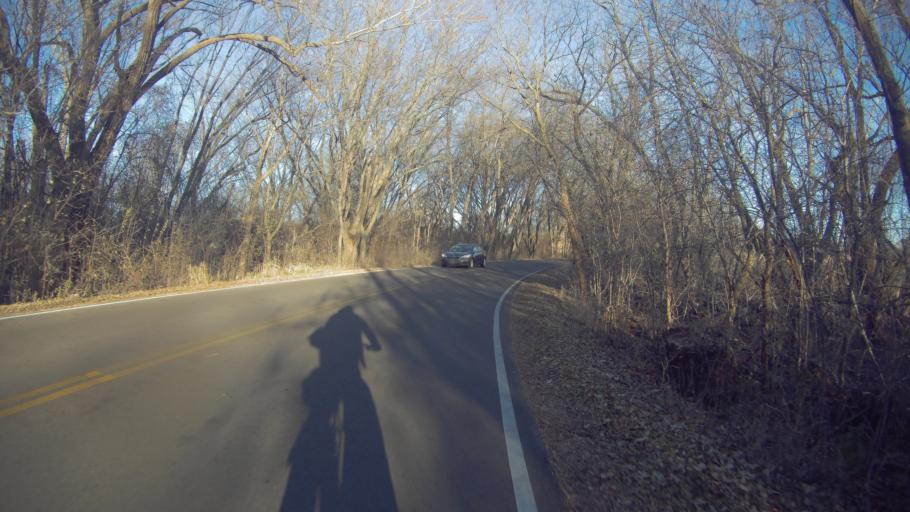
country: US
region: Wisconsin
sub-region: Dane County
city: Madison
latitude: 43.0561
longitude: -89.4085
